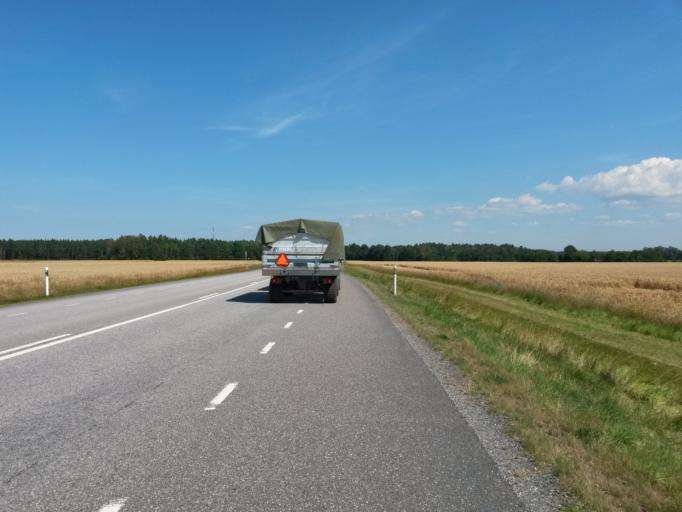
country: SE
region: Vaestra Goetaland
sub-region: Lidkopings Kommun
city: Lidkoping
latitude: 58.4835
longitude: 13.1187
